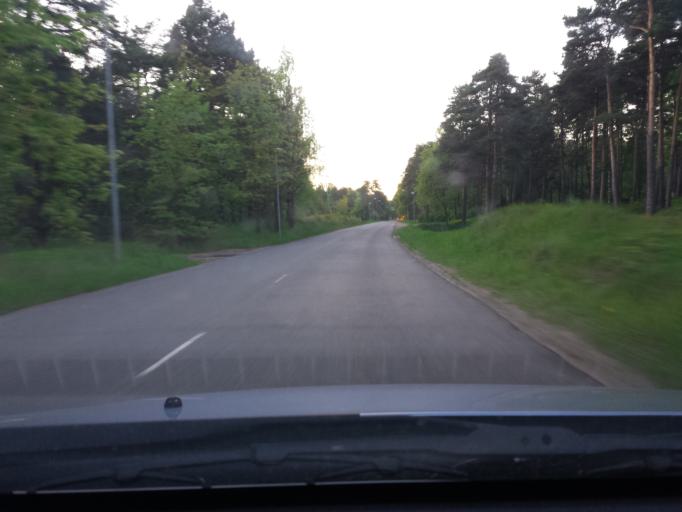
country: LV
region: Riga
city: Riga
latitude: 56.9911
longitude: 24.1407
